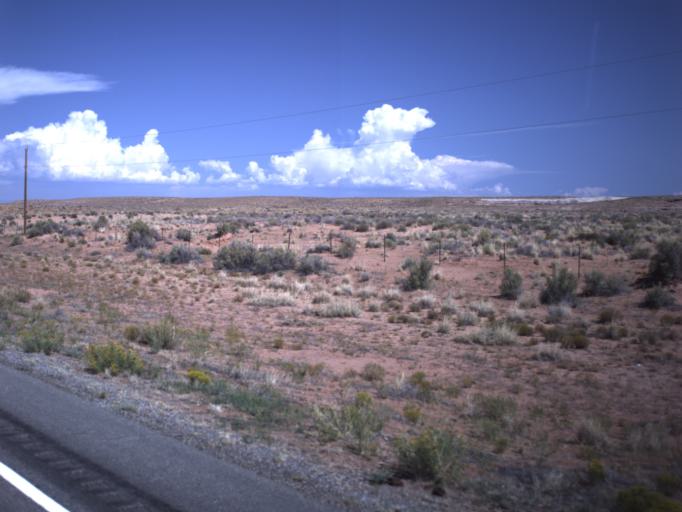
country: US
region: Utah
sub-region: San Juan County
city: Blanding
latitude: 37.1348
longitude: -109.5539
